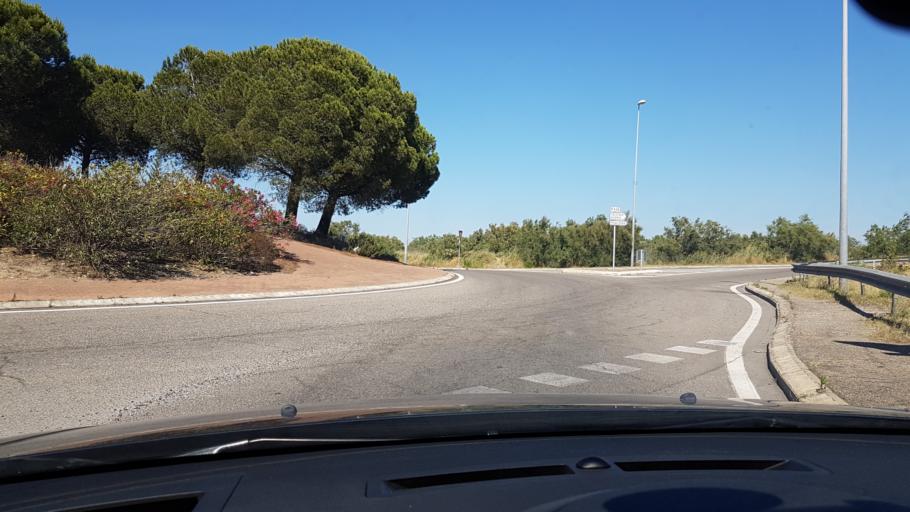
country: FR
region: Provence-Alpes-Cote d'Azur
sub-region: Departement des Bouches-du-Rhone
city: Port-Saint-Louis-du-Rhone
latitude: 43.3933
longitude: 4.8152
